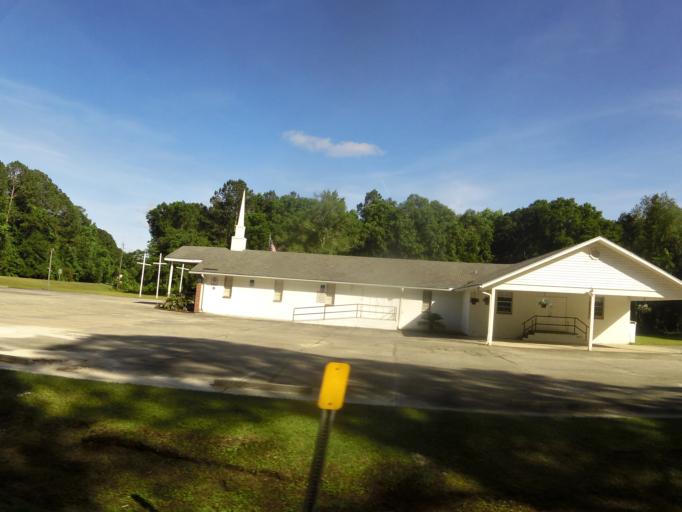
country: US
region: Florida
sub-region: Nassau County
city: Nassau Village-Ratliff
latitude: 30.5197
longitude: -81.7681
